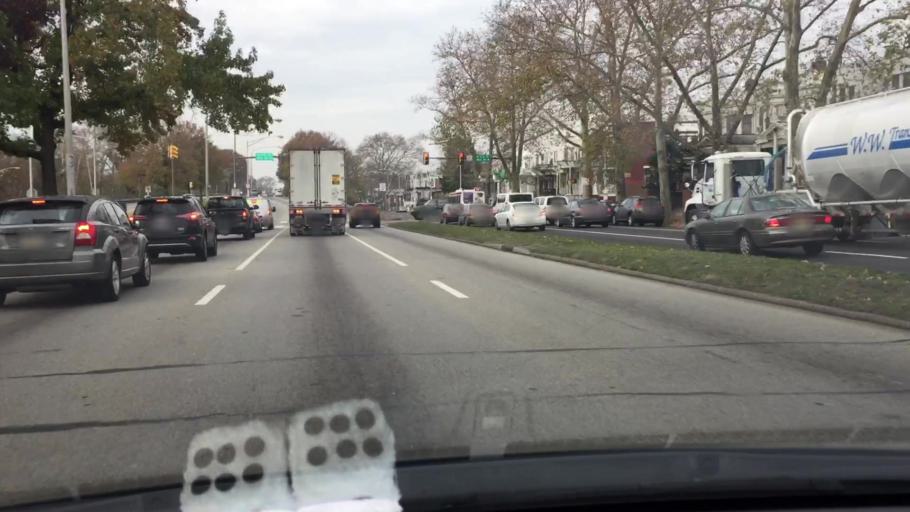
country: US
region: Pennsylvania
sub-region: Montgomery County
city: Rockledge
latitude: 40.0248
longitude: -75.1296
